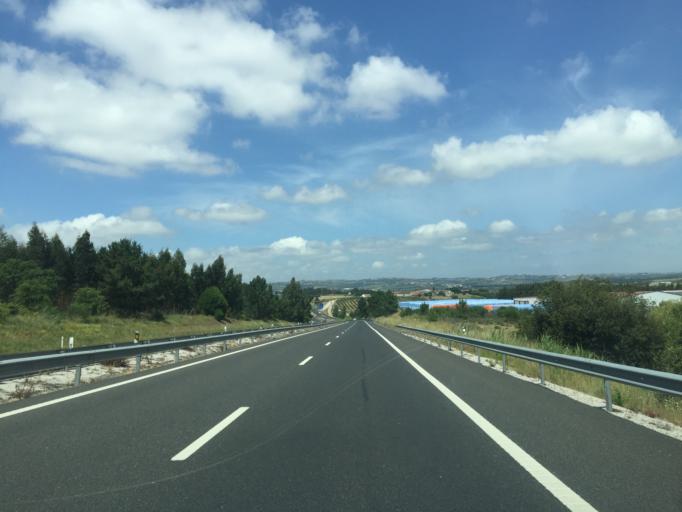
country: PT
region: Leiria
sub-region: Bombarral
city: Bombarral
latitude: 39.2428
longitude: -9.1693
